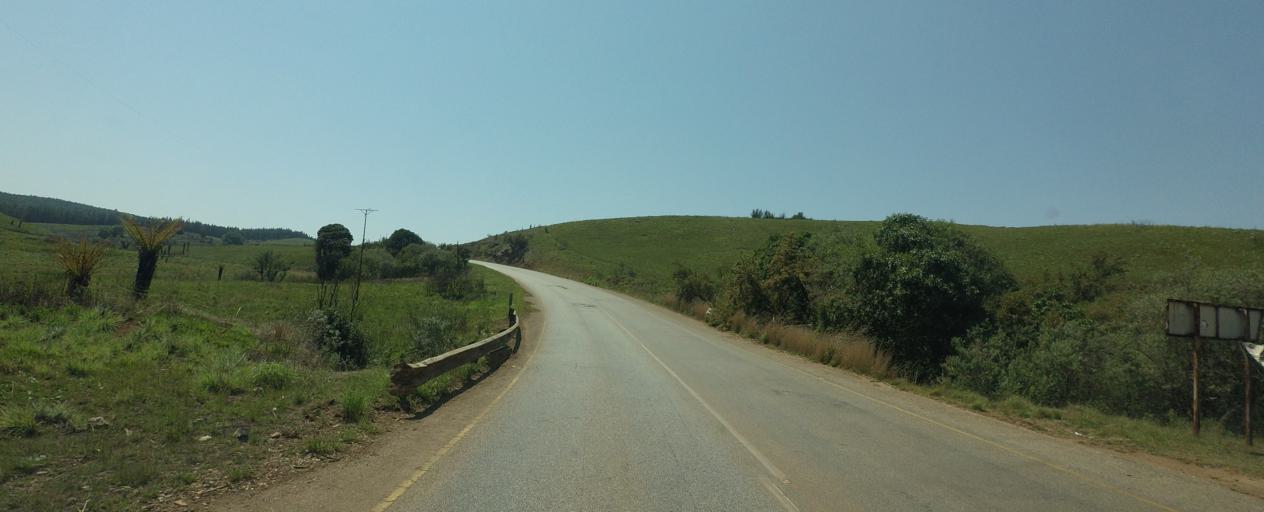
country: ZA
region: Mpumalanga
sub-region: Ehlanzeni District
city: Graksop
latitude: -24.9255
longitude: 30.8303
